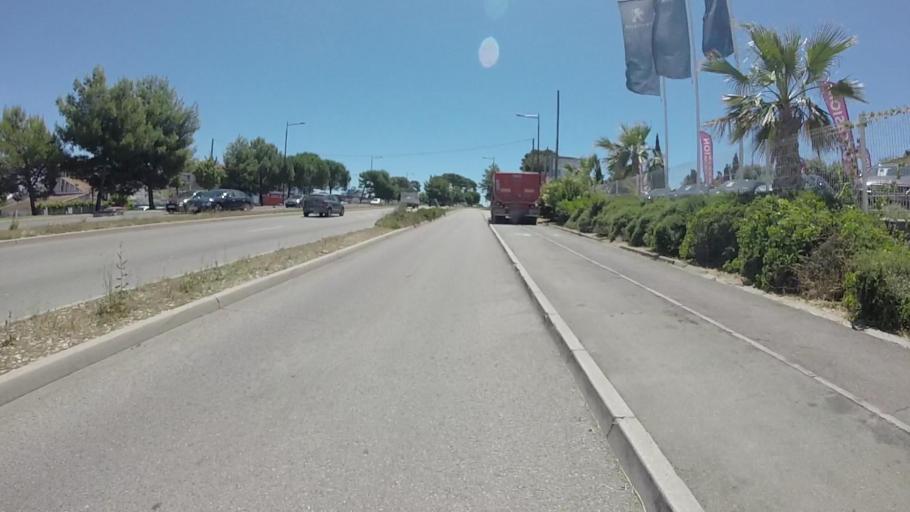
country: FR
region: Provence-Alpes-Cote d'Azur
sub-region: Departement des Alpes-Maritimes
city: Biot
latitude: 43.5978
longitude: 7.0883
